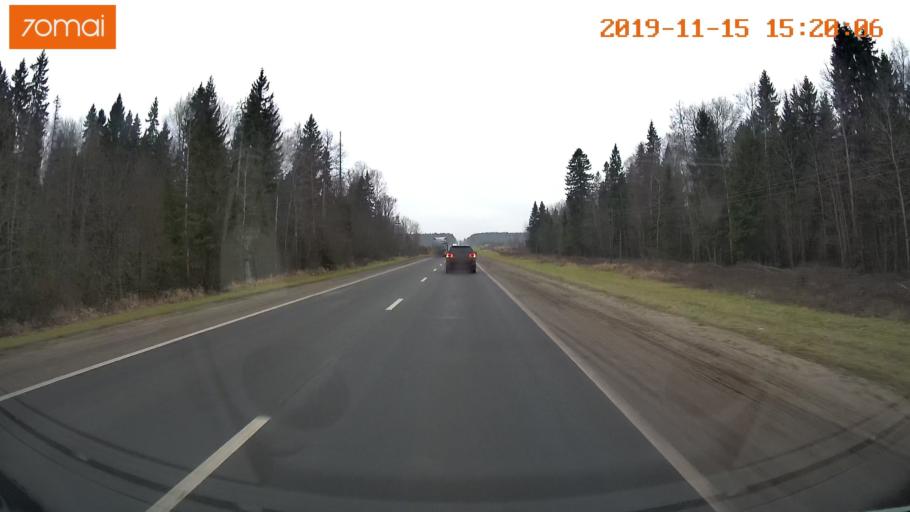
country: RU
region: Jaroslavl
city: Danilov
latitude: 58.2273
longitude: 40.1672
